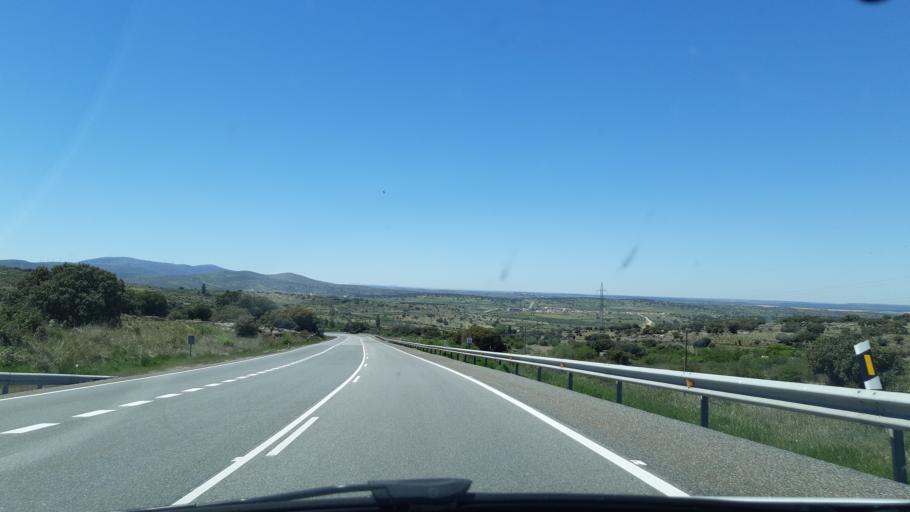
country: ES
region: Castille and Leon
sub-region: Provincia de Segovia
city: Vegas de Matute
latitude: 40.7502
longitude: -4.2884
